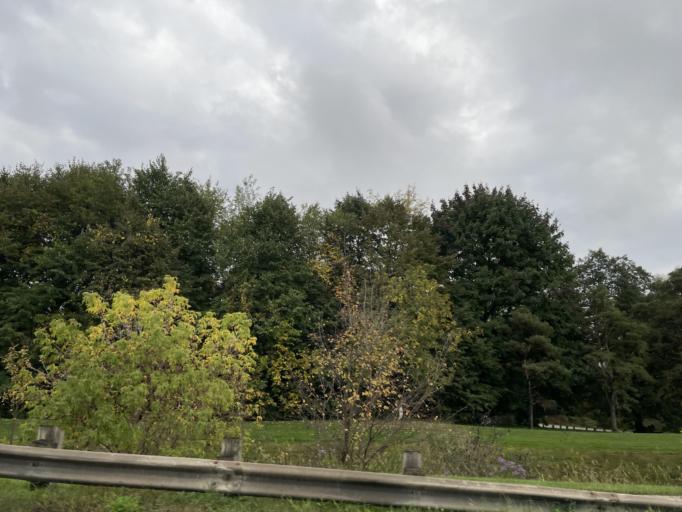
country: CA
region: Ontario
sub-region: Wellington County
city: Guelph
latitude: 43.5686
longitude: -80.2725
